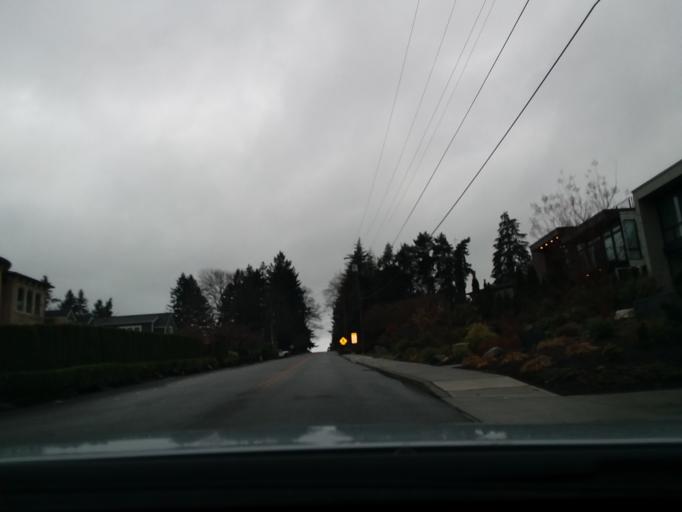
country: US
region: Washington
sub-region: King County
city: Clyde Hill
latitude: 47.6230
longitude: -122.2099
